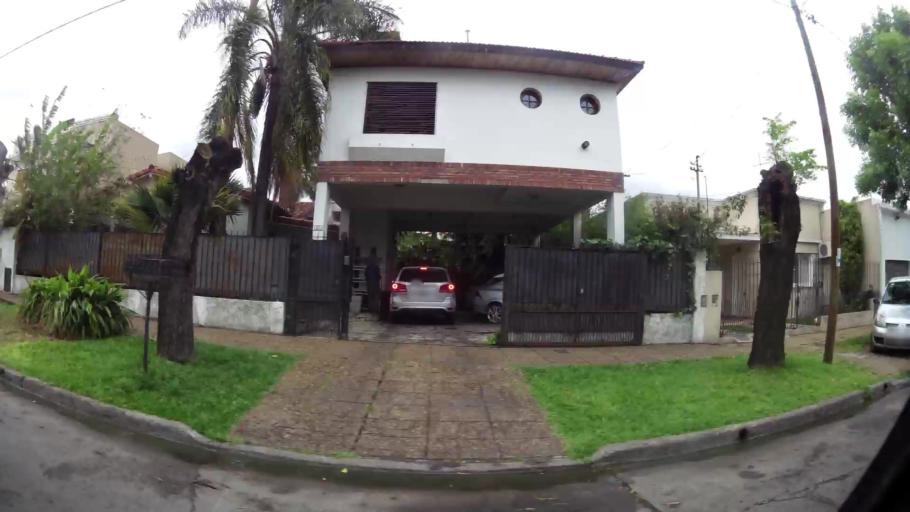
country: AR
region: Buenos Aires
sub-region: Partido de Lomas de Zamora
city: Lomas de Zamora
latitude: -34.7459
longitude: -58.3779
